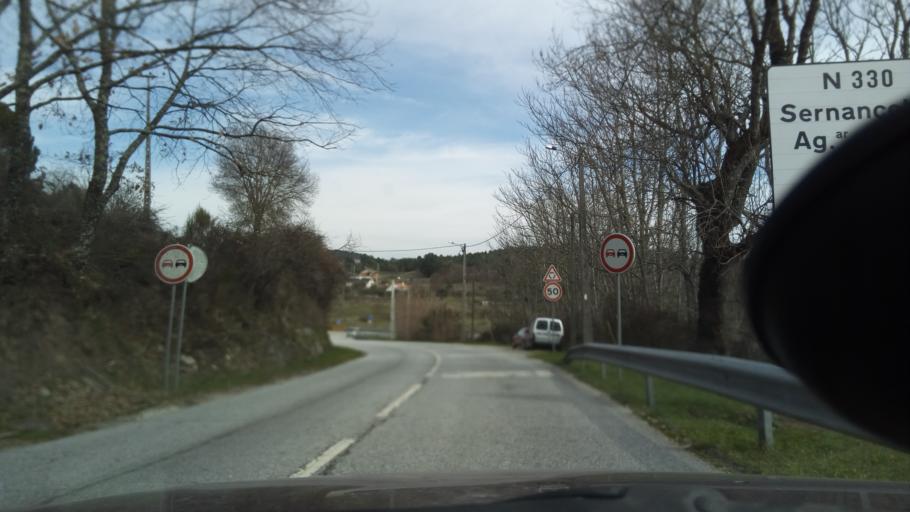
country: PT
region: Guarda
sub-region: Fornos de Algodres
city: Fornos de Algodres
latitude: 40.6130
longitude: -7.5245
